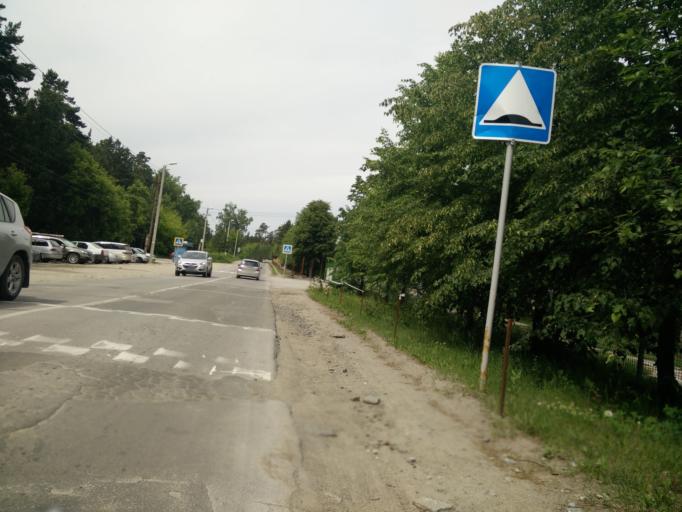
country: RU
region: Novosibirsk
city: Berdsk
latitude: 54.7860
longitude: 83.0519
